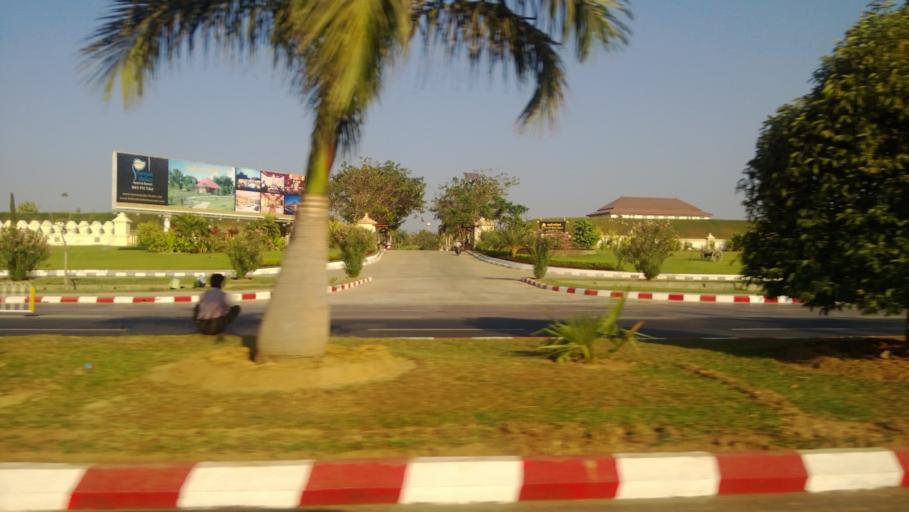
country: MM
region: Mandalay
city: Nay Pyi Taw
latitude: 19.7187
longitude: 96.1116
